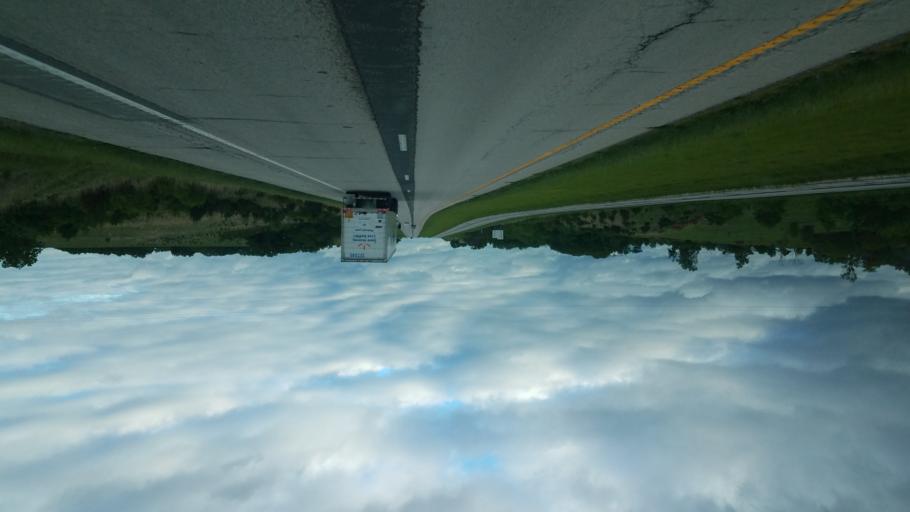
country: US
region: Missouri
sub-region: Harrison County
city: Bethany
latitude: 40.3884
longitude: -93.9989
